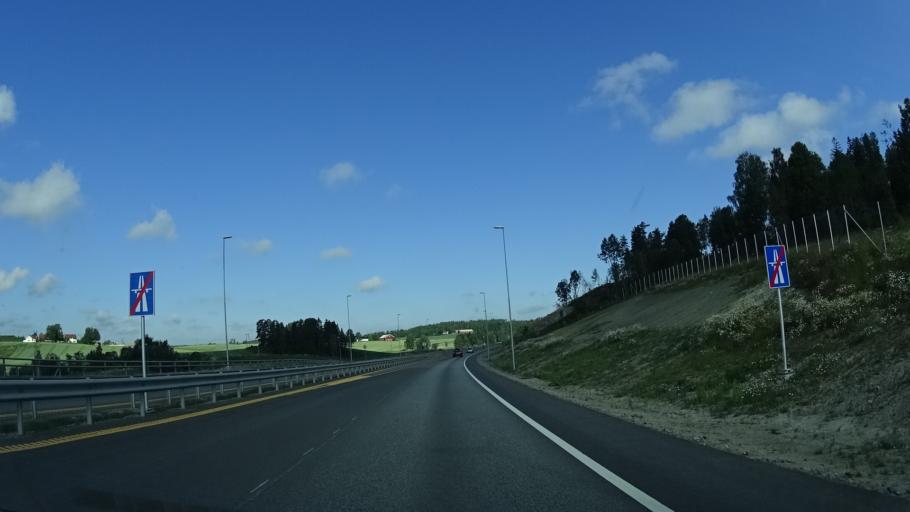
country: NO
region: Ostfold
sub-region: Hobol
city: Elvestad
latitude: 59.6432
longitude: 10.9305
